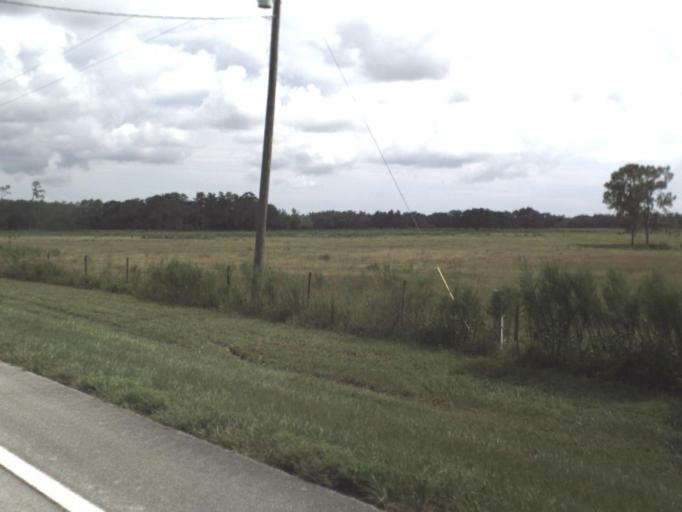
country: US
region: Florida
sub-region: DeSoto County
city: Nocatee
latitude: 27.2051
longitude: -82.0020
